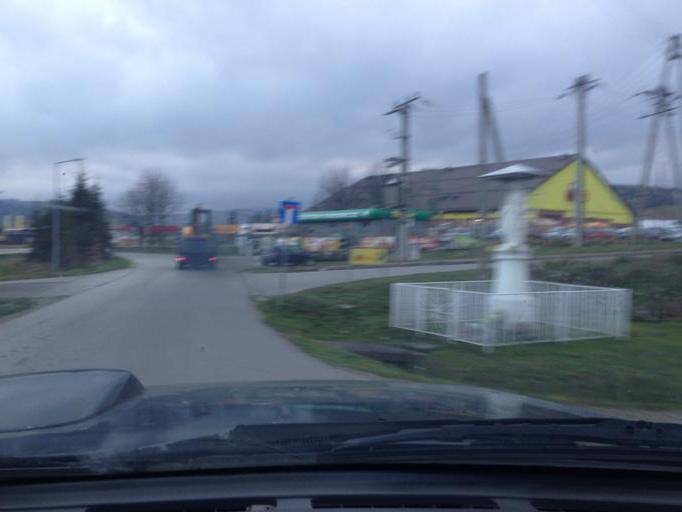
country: PL
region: Subcarpathian Voivodeship
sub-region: Powiat jasielski
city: Nowy Zmigrod
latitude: 49.6085
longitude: 21.5195
